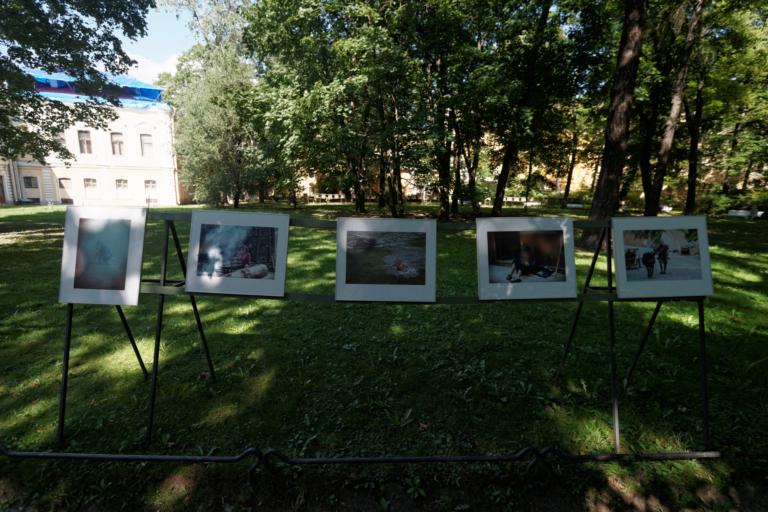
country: RU
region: St.-Petersburg
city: Centralniy
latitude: 59.9363
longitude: 30.3460
